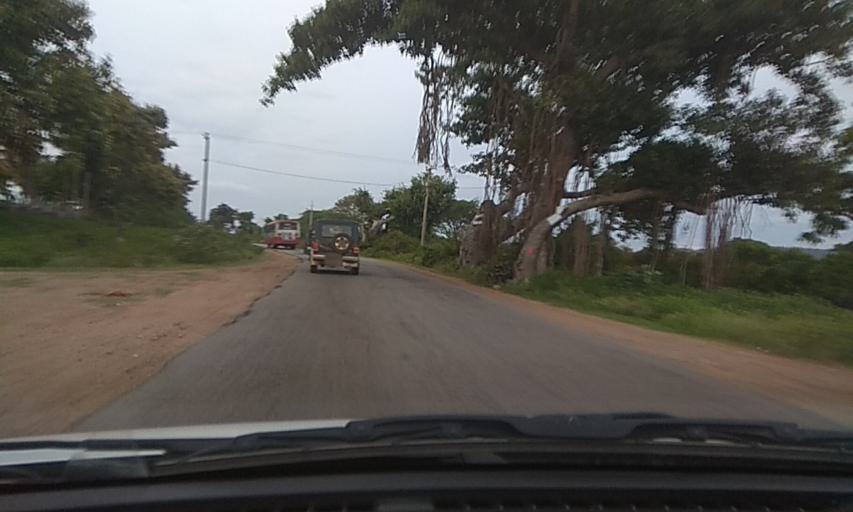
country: IN
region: Karnataka
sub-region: Chamrajnagar
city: Gundlupet
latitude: 11.8128
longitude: 76.7727
